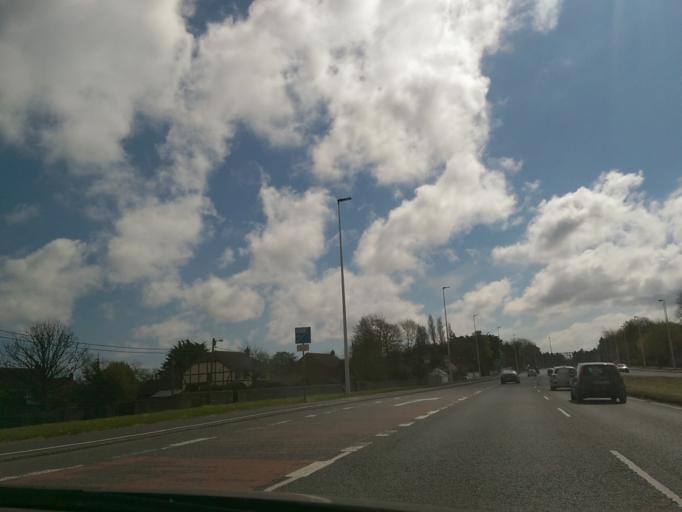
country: IE
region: Leinster
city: Mount Merrion
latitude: 53.3075
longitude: -6.2142
